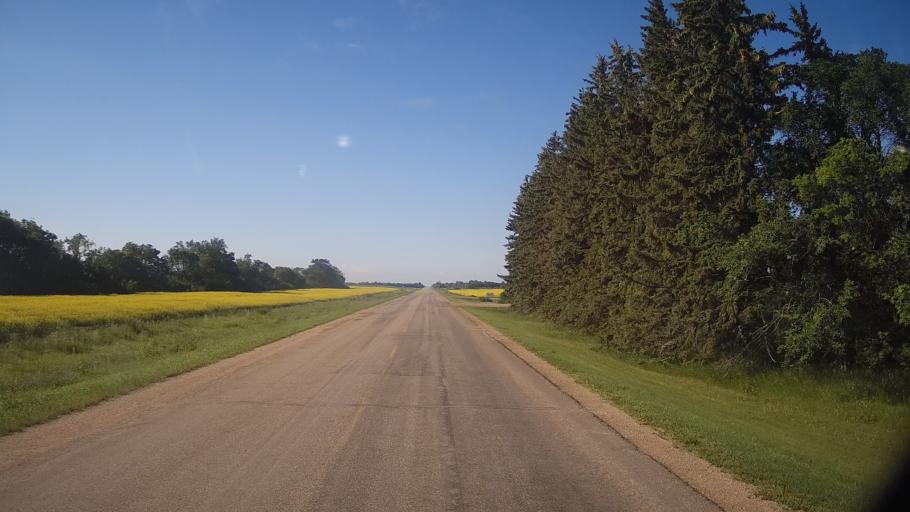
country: CA
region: Saskatchewan
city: Watrous
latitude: 51.8162
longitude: -105.2866
